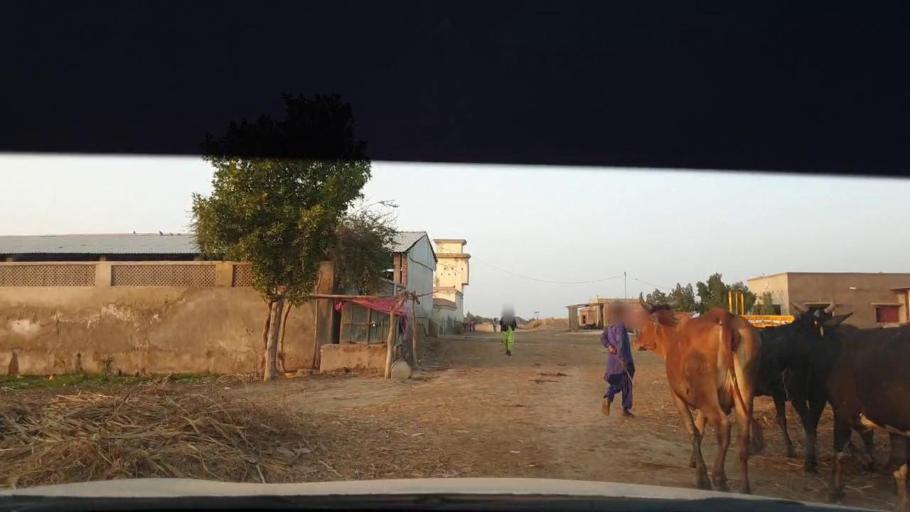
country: PK
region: Sindh
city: Berani
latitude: 25.7546
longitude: 69.0073
